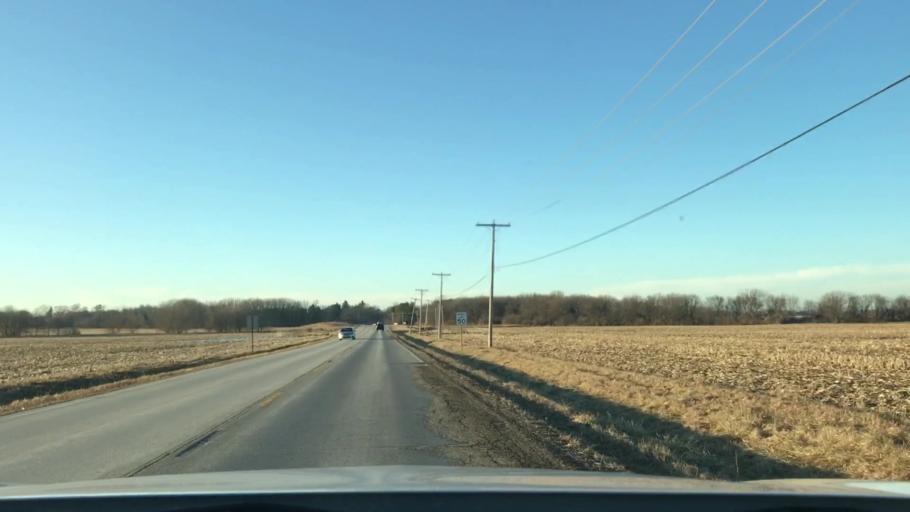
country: US
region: Illinois
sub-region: Kane County
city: Gilberts
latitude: 42.0856
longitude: -88.3898
